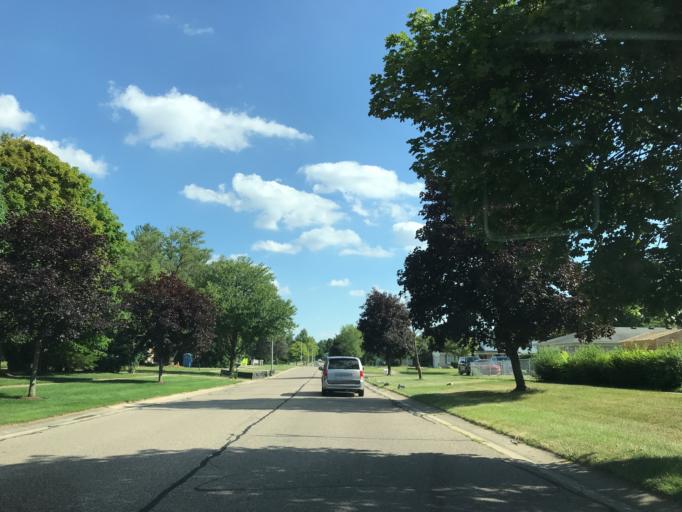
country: US
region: Michigan
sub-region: Oakland County
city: Farmington
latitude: 42.4185
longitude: -83.3942
